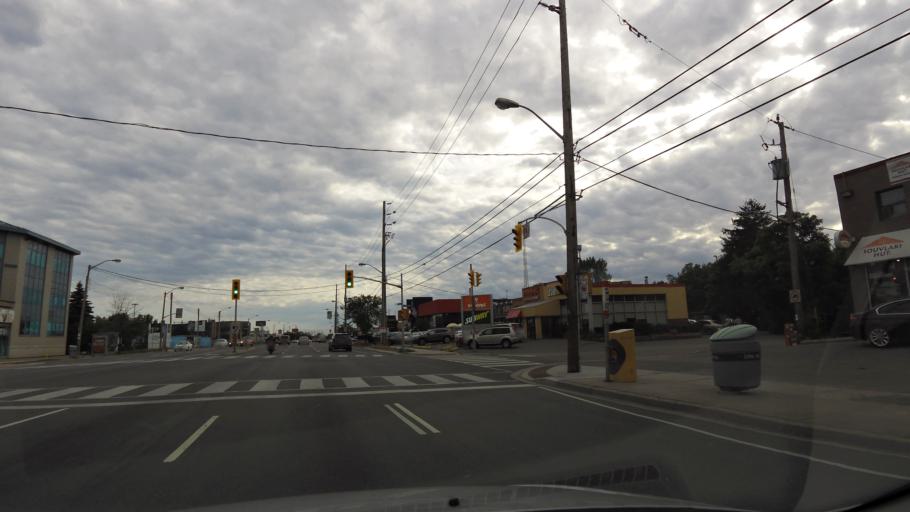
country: CA
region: Ontario
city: Etobicoke
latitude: 43.6364
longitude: -79.5399
